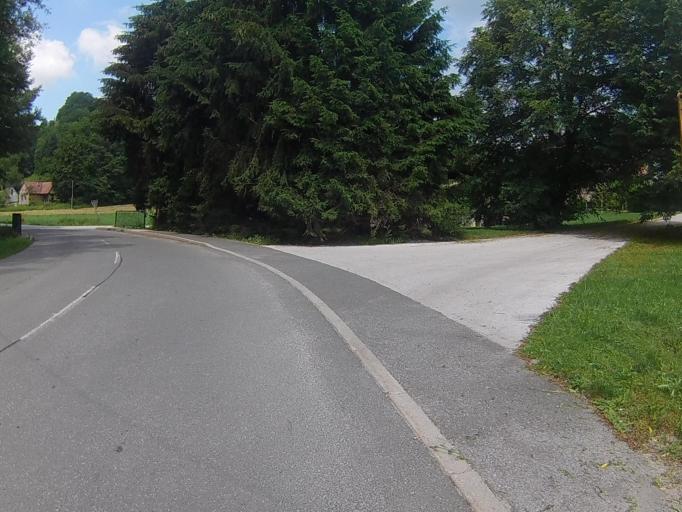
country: SI
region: Kungota
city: Zgornja Kungota
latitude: 46.6114
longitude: 15.6262
